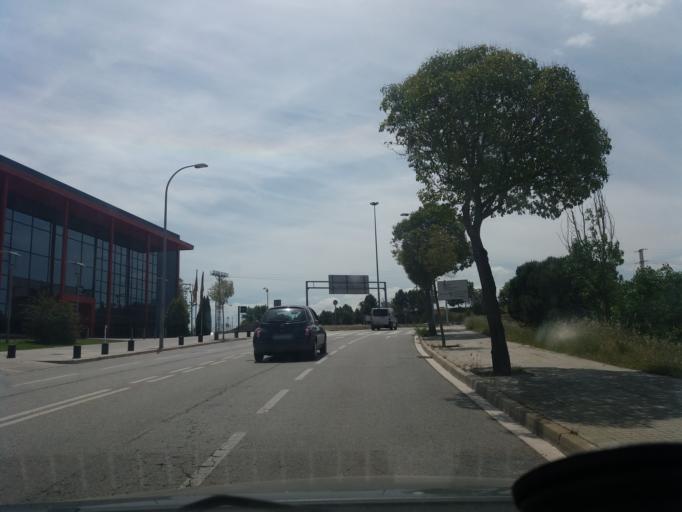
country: ES
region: Catalonia
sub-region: Provincia de Barcelona
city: Manresa
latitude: 41.7222
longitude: 1.8475
